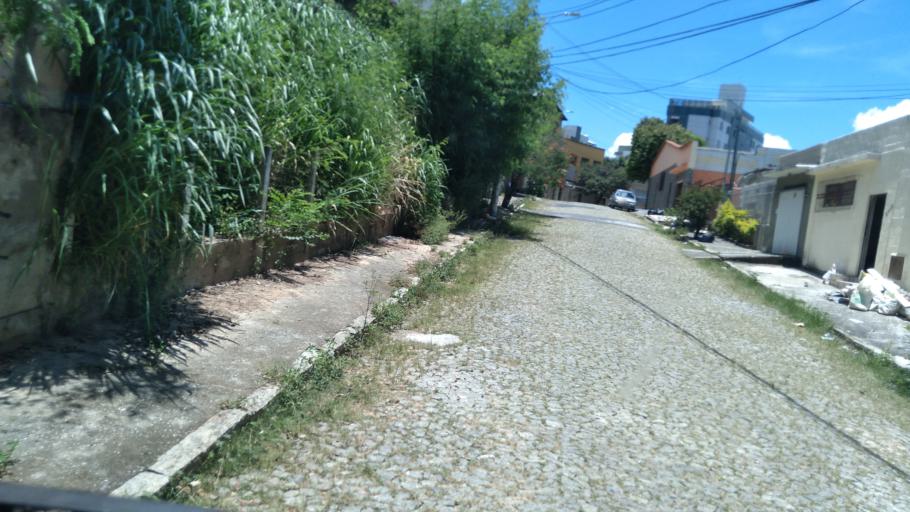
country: BR
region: Minas Gerais
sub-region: Belo Horizonte
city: Belo Horizonte
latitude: -19.9191
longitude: -43.9895
